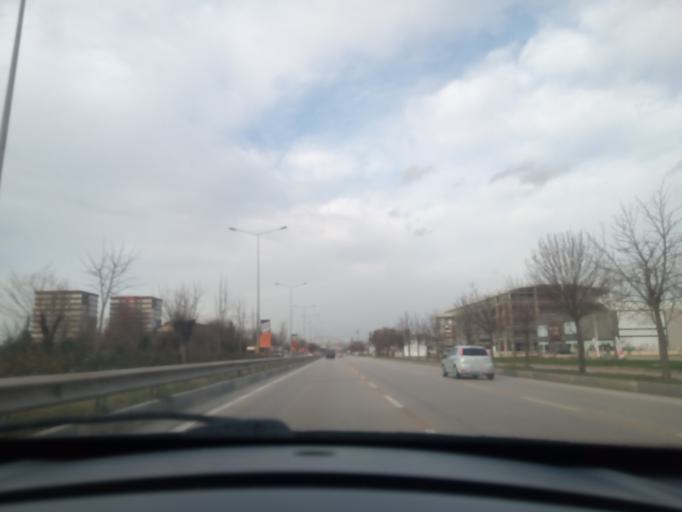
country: TR
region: Bursa
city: Cali
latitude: 40.2129
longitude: 28.9271
